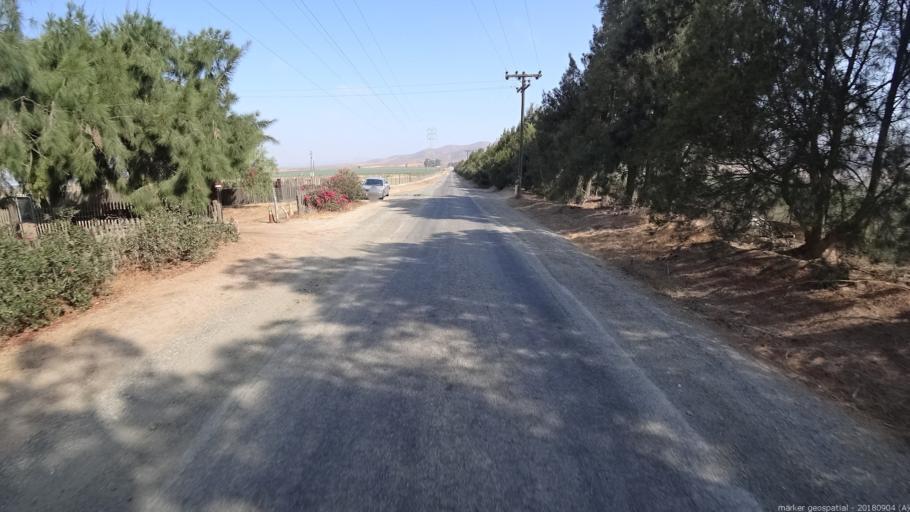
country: US
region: California
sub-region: Monterey County
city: Soledad
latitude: 36.4557
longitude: -121.3318
